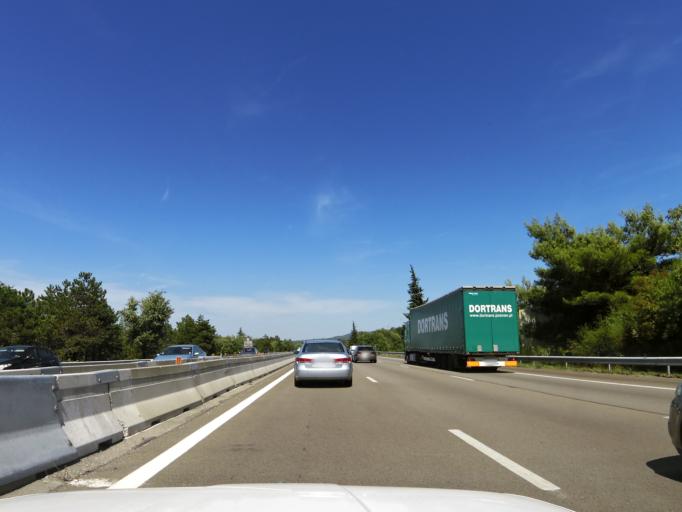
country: FR
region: Rhone-Alpes
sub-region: Departement de l'Ardeche
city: Cruas
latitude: 44.6514
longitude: 4.7940
